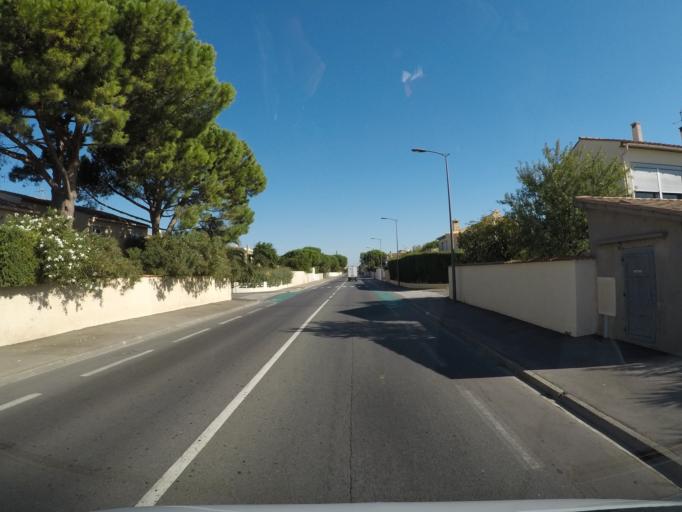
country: FR
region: Languedoc-Roussillon
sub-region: Departement de l'Aude
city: Narbonne
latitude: 43.1764
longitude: 3.0111
